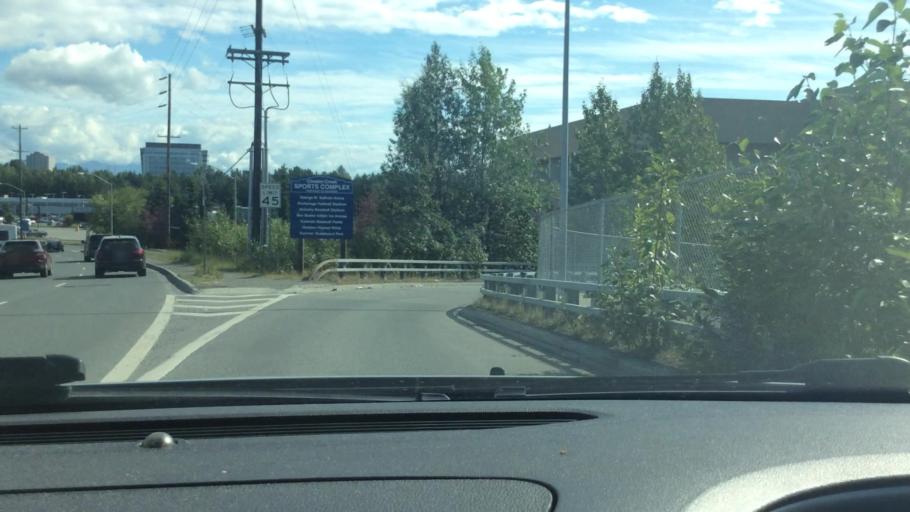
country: US
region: Alaska
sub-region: Anchorage Municipality
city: Anchorage
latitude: 61.2064
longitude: -149.8713
